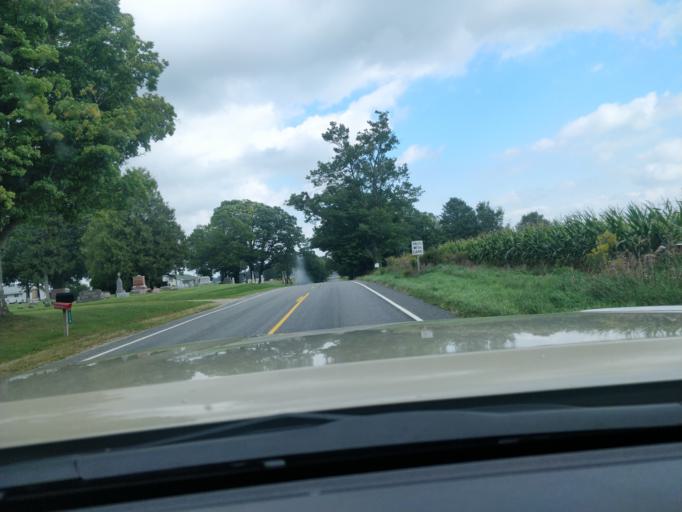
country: US
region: Michigan
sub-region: Kent County
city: Lowell
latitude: 42.8860
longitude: -85.2791
